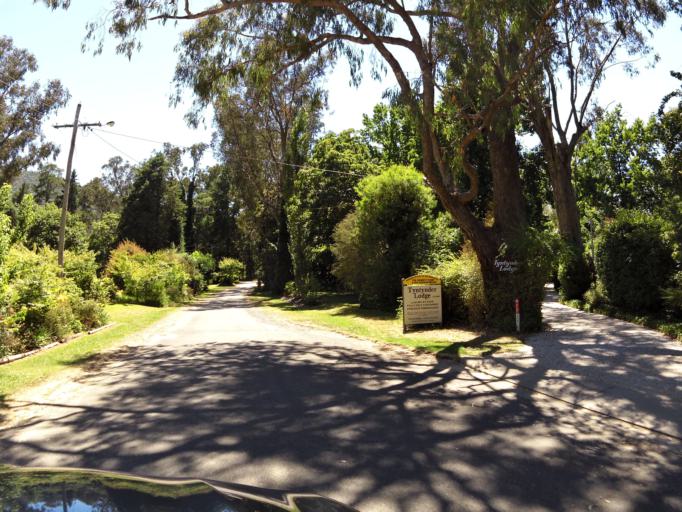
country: AU
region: Victoria
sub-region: Alpine
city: Mount Beauty
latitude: -36.7291
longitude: 146.9796
